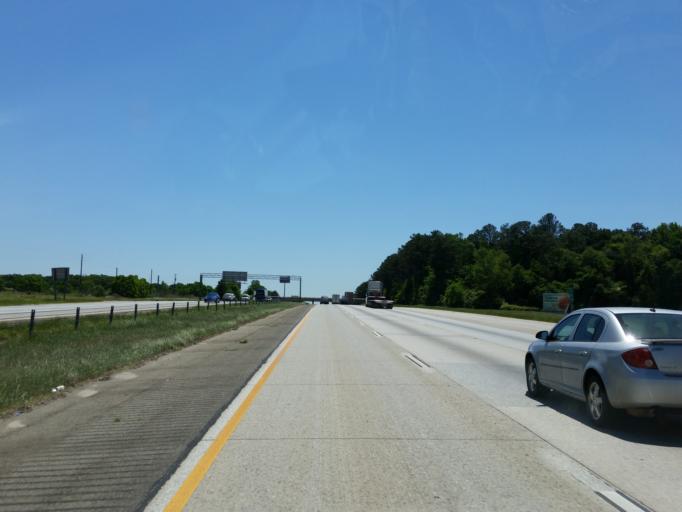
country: US
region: Georgia
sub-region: Houston County
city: Centerville
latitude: 32.5822
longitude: -83.7434
